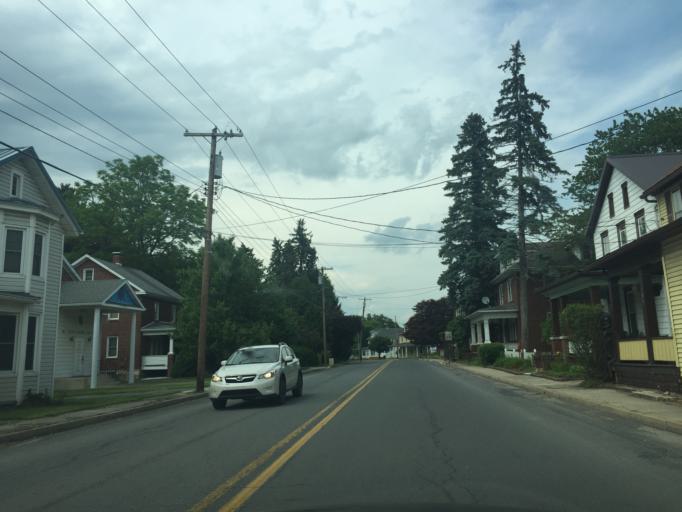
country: US
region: Pennsylvania
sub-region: Fulton County
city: McConnellsburg
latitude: 39.9352
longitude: -77.9976
